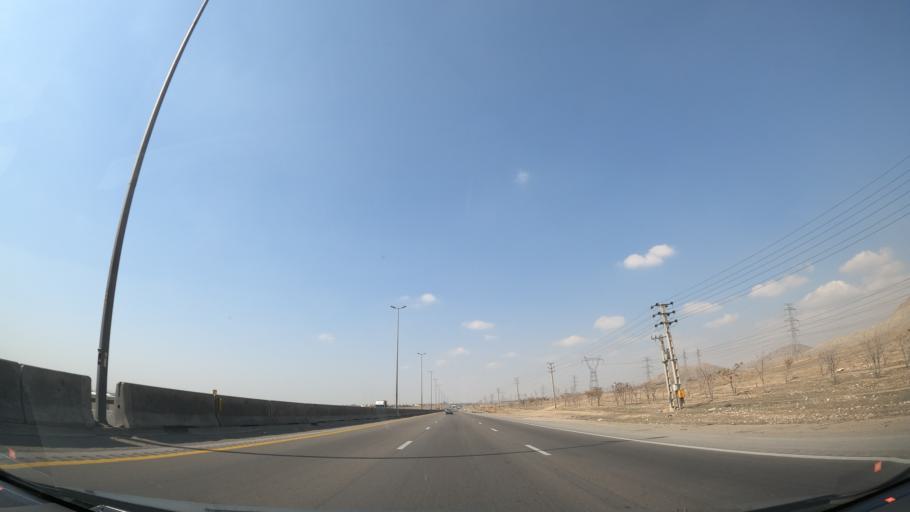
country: IR
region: Qazvin
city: Abyek
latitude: 36.0580
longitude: 50.5030
